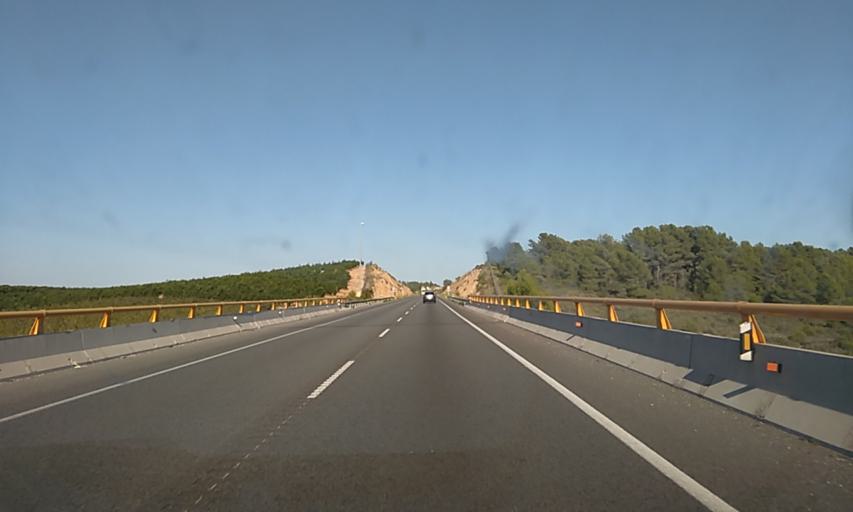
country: ES
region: Valencia
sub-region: Provincia de Castello
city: Torreblanca
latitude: 40.2138
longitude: 0.1497
